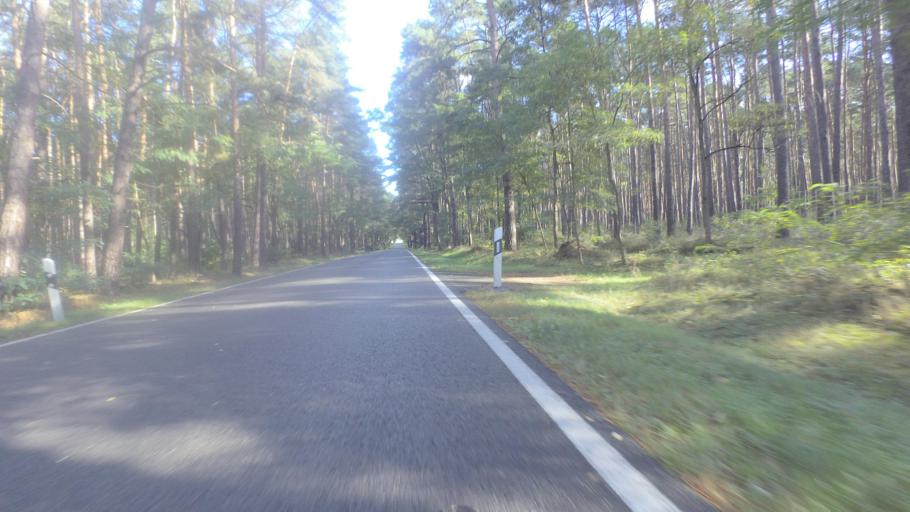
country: DE
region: Brandenburg
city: Niedergorsdorf
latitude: 51.8764
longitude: 13.0488
